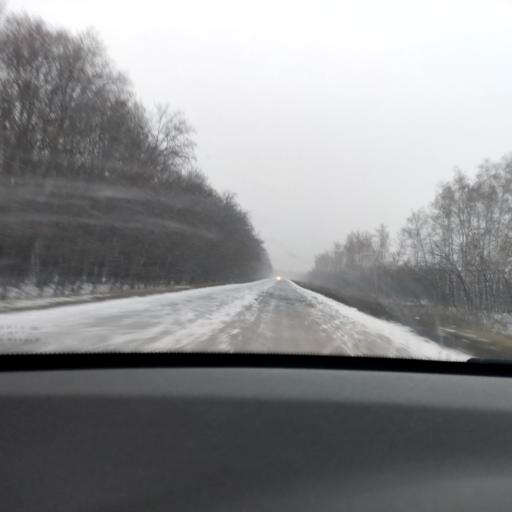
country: RU
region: Samara
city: Novokuybyshevsk
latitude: 52.9674
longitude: 49.8887
